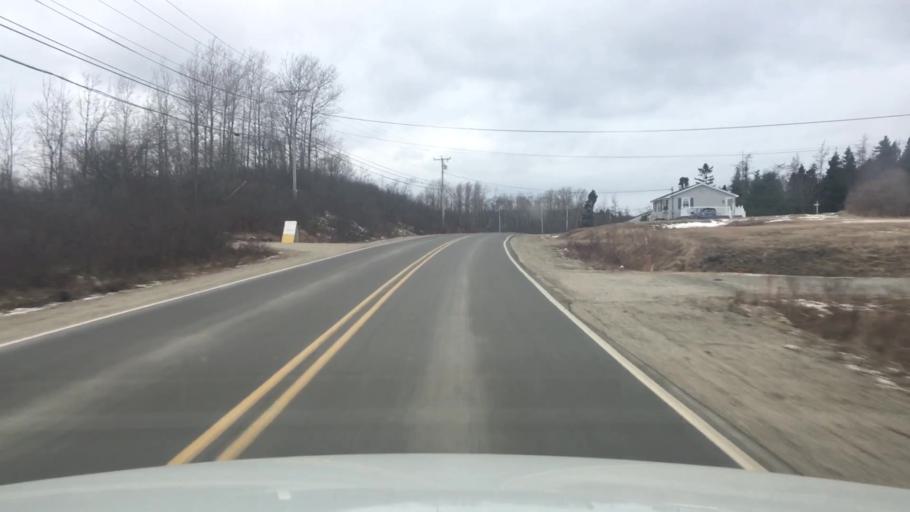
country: US
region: Maine
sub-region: Washington County
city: Jonesport
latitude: 44.5518
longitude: -67.6229
